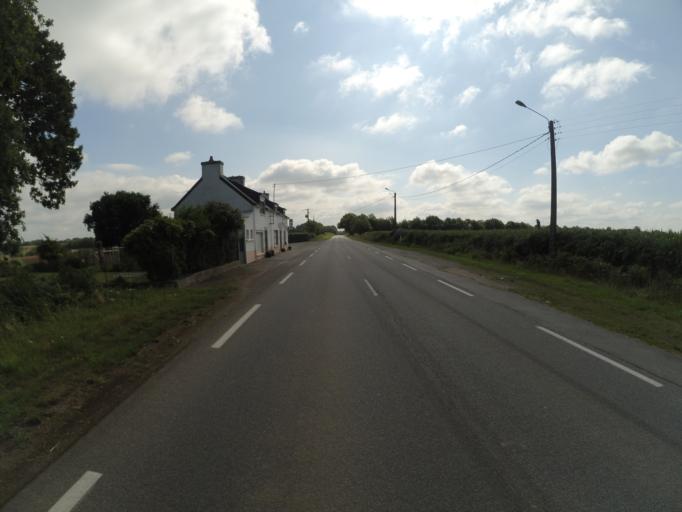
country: FR
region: Brittany
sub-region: Departement du Finistere
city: Le Trevoux
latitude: 47.9220
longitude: -3.6448
